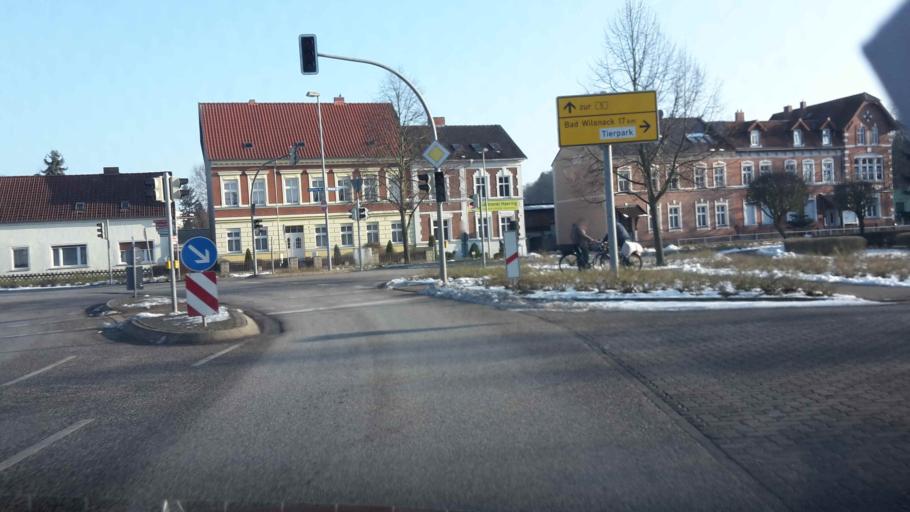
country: DE
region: Brandenburg
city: Perleberg
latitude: 53.0698
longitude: 11.8582
